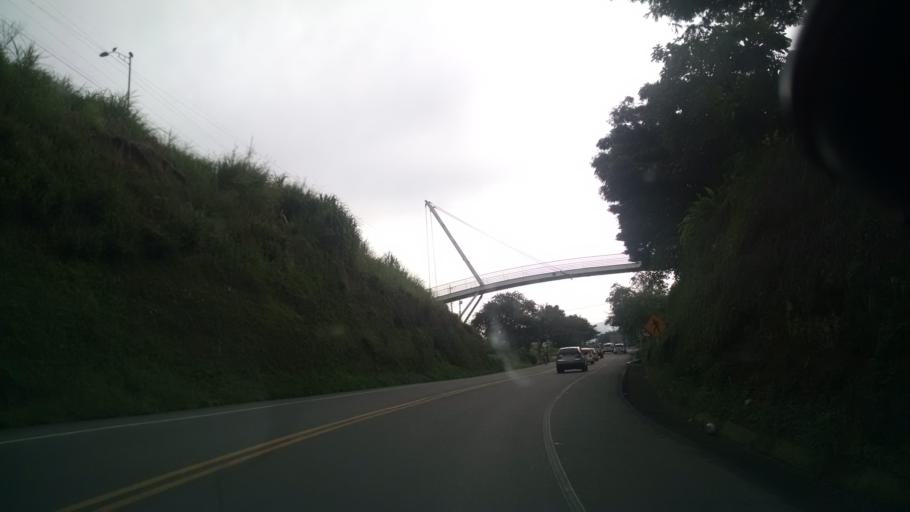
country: CO
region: Risaralda
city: Pereira
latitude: 4.8208
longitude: -75.7272
